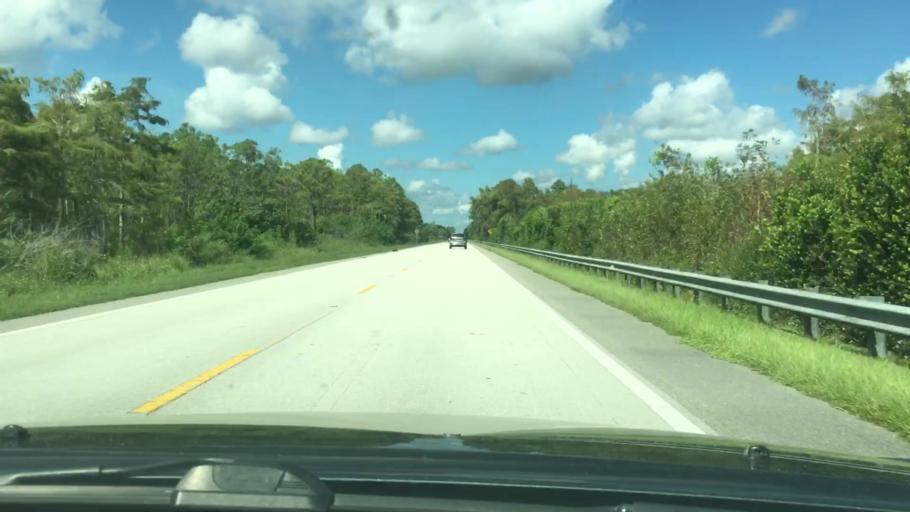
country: US
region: Florida
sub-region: Collier County
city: Lely Resort
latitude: 25.8705
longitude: -81.1670
